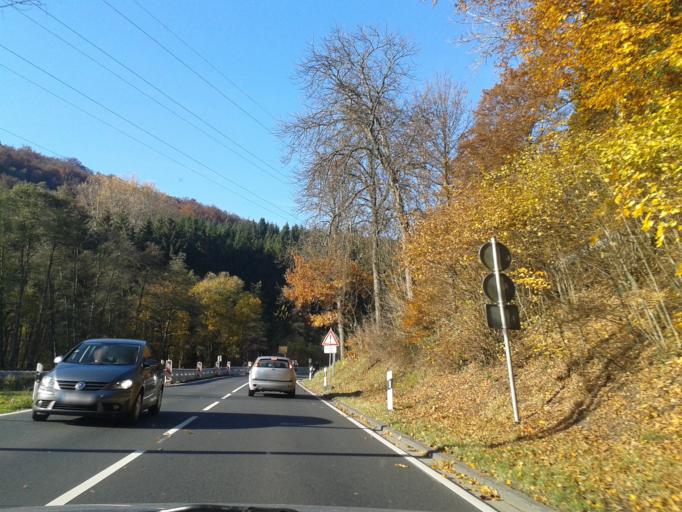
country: DE
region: North Rhine-Westphalia
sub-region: Regierungsbezirk Arnsberg
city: Bad Laasphe
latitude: 50.9443
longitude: 8.3756
